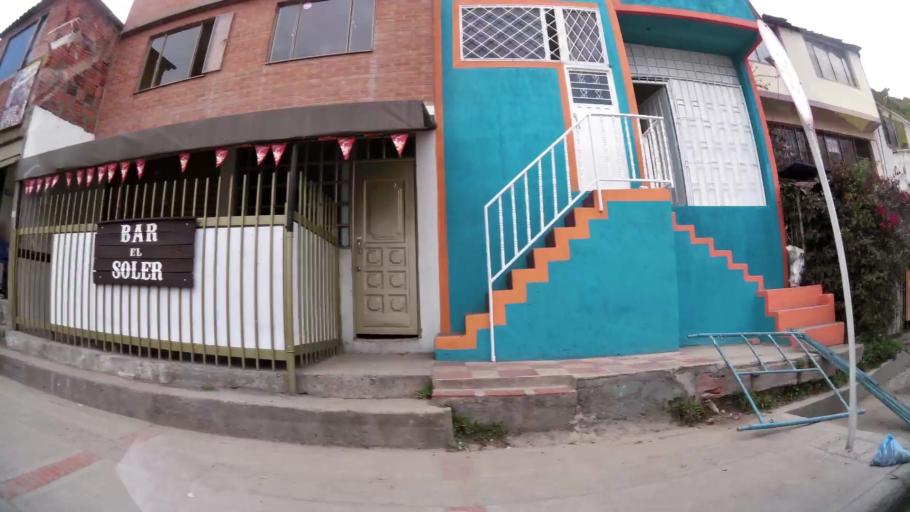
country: CO
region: Cundinamarca
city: La Calera
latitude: 4.7648
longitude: -74.0276
